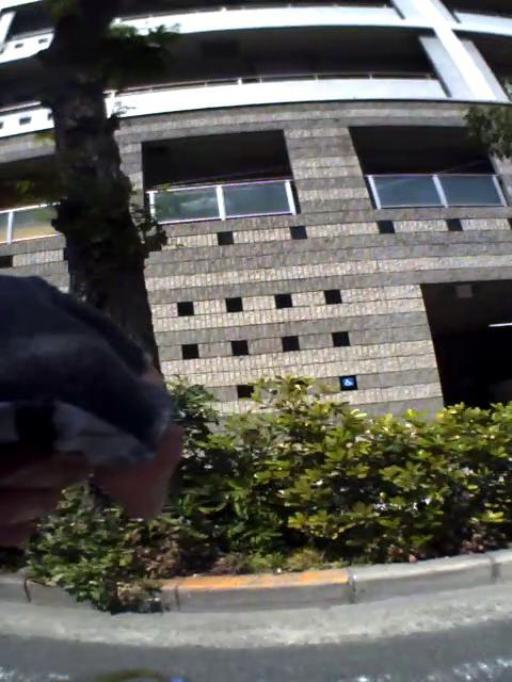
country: JP
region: Osaka
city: Osaka-shi
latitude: 34.6779
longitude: 135.5171
